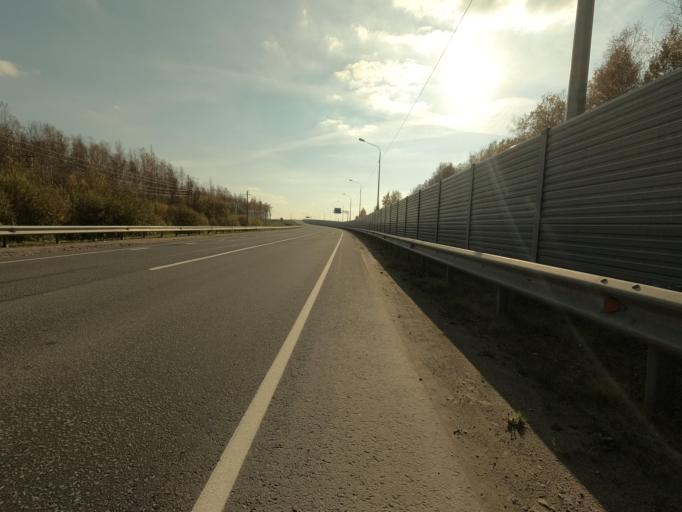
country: RU
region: Leningrad
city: Mga
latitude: 59.7627
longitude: 31.0943
